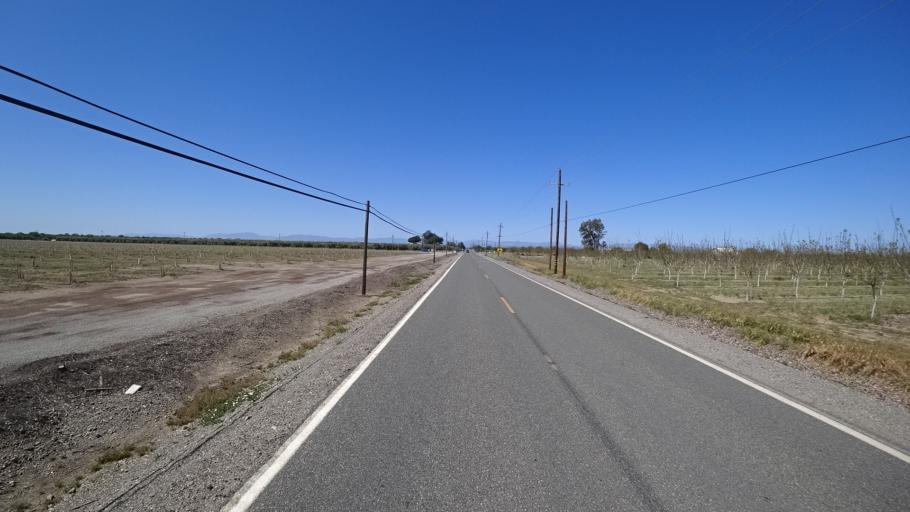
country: US
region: California
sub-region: Glenn County
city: Orland
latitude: 39.7106
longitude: -122.1380
